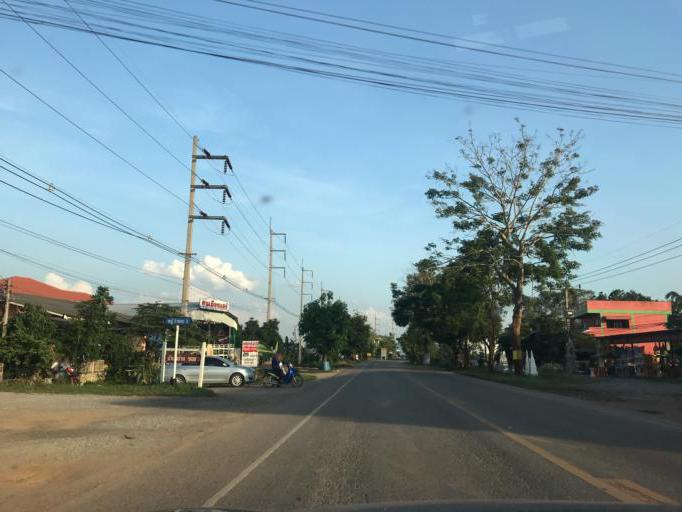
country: TH
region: Phayao
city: Chiang Kham
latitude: 19.5263
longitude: 100.2944
